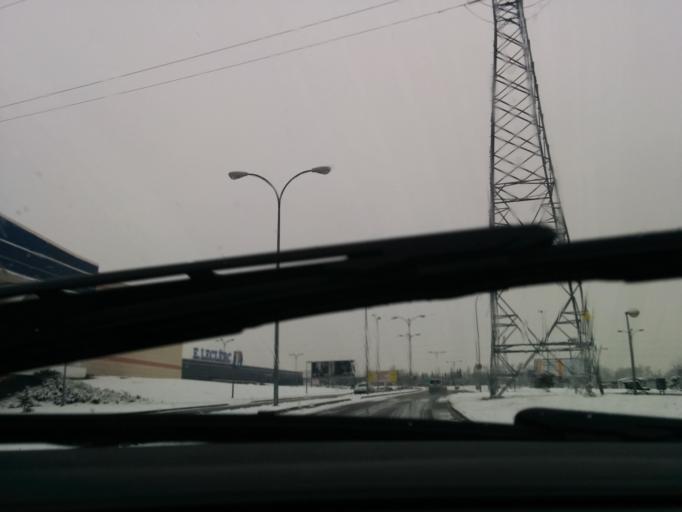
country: ES
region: Navarre
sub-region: Provincia de Navarra
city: Segundo Ensanche
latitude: 42.7849
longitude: -1.6326
